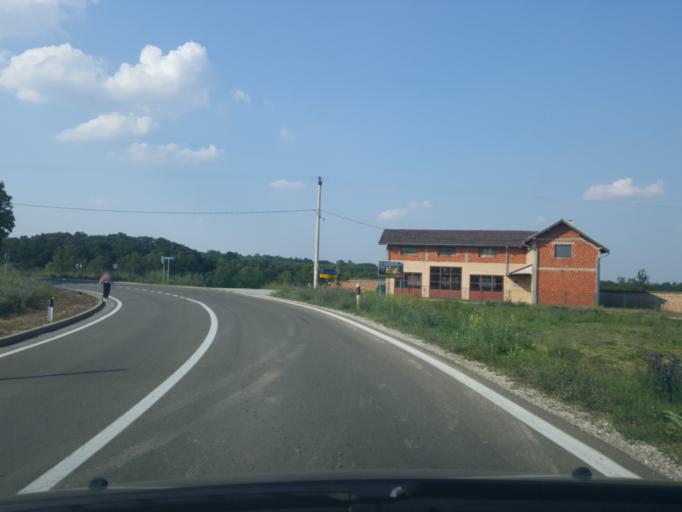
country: RS
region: Central Serbia
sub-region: Sumadijski Okrug
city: Topola
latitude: 44.3187
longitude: 20.7028
